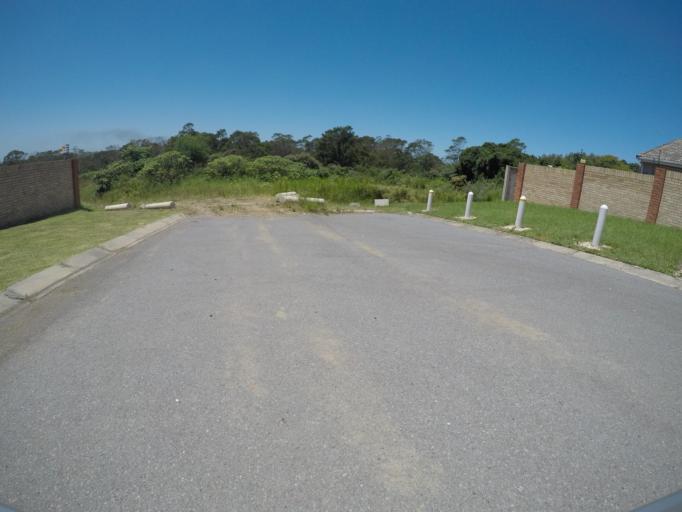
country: ZA
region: Eastern Cape
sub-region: Buffalo City Metropolitan Municipality
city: East London
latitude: -32.9543
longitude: 27.9420
